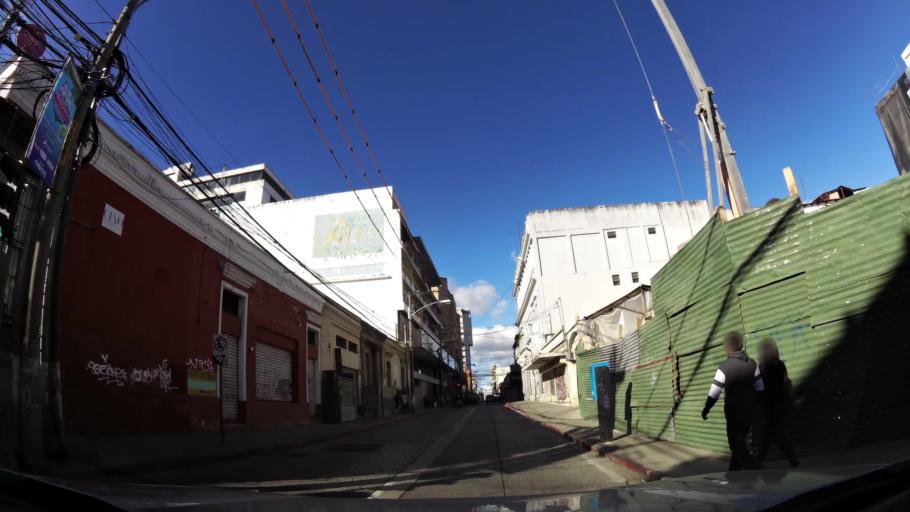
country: GT
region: Guatemala
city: Guatemala City
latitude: 14.6380
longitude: -90.5131
